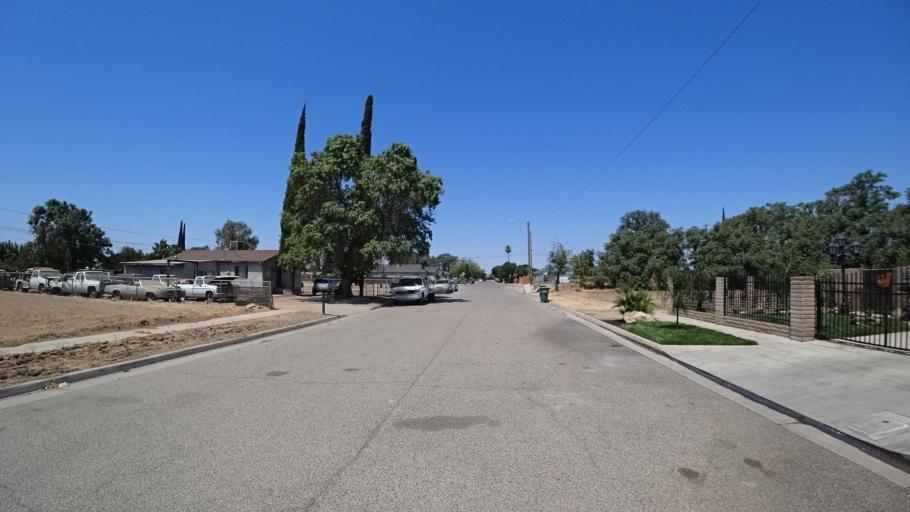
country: US
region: California
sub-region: Fresno County
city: West Park
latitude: 36.7096
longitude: -119.8124
